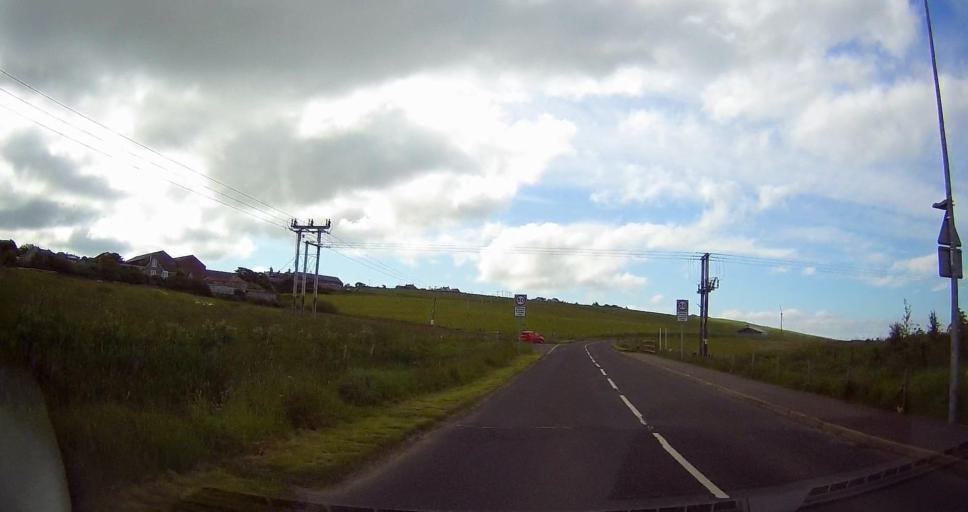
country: GB
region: Scotland
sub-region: Orkney Islands
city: Orkney
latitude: 58.9725
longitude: -2.9622
